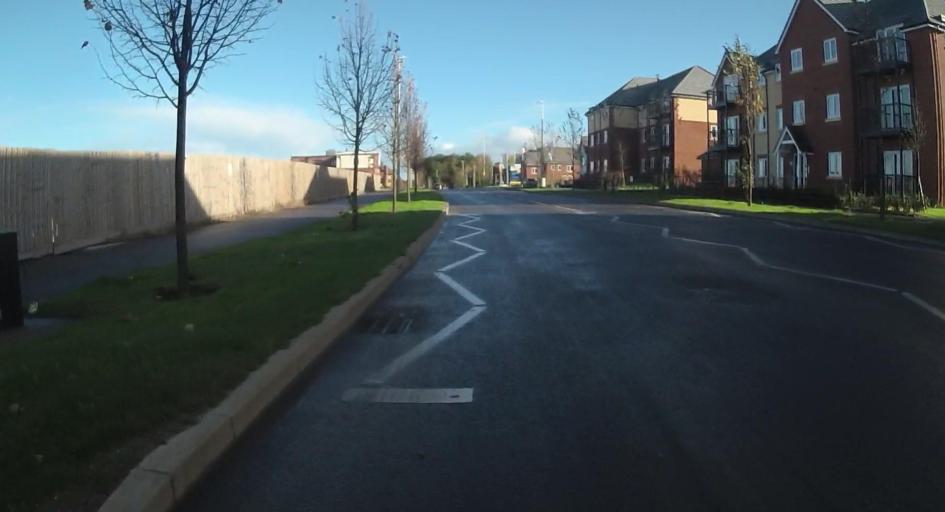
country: GB
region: England
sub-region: Wokingham
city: Wokingham
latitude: 51.4242
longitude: -0.8441
